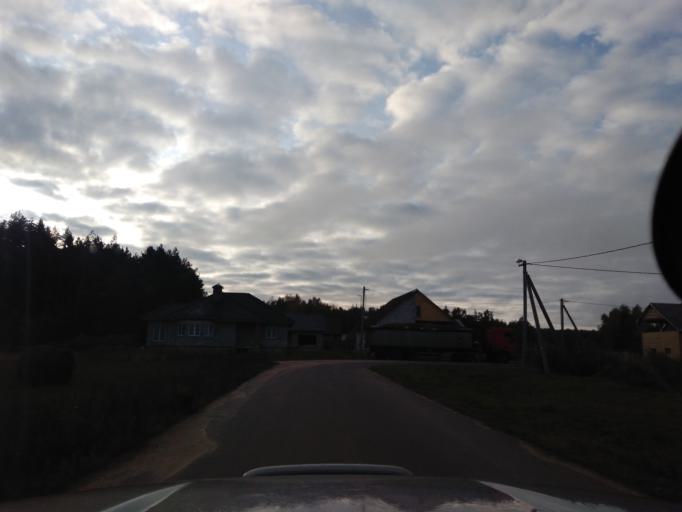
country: BY
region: Minsk
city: Kapyl'
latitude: 53.1624
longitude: 27.1037
